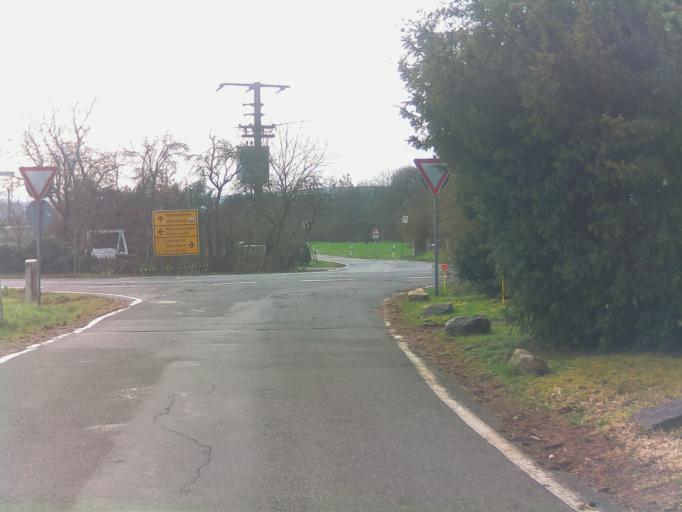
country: DE
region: Rheinland-Pfalz
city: Ippenschied
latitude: 49.8873
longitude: 7.6272
